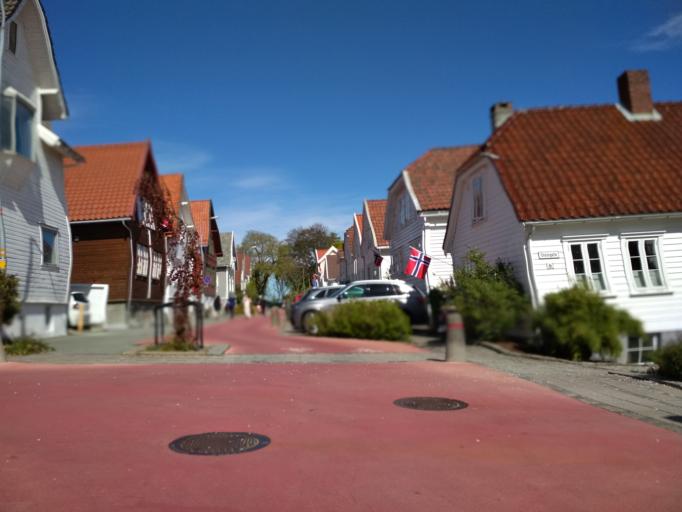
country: NO
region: Rogaland
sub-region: Stavanger
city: Stavanger
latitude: 58.9701
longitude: 5.7233
